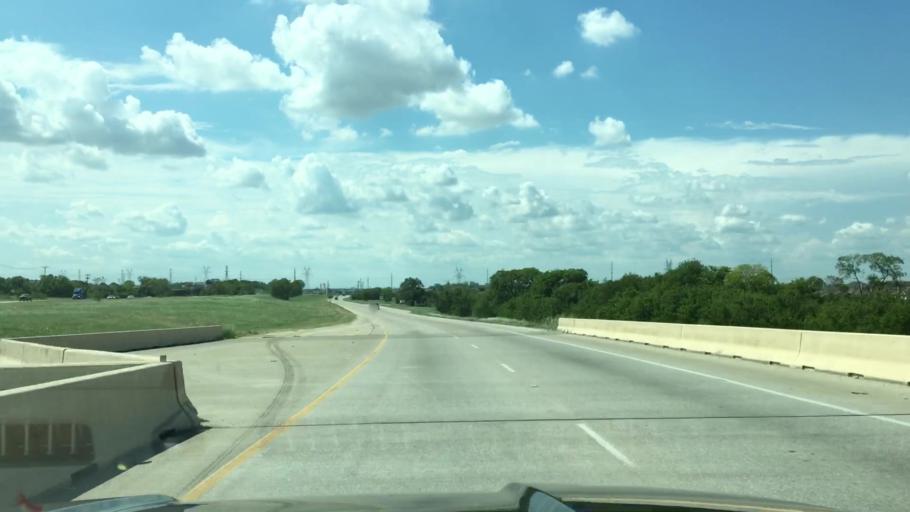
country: US
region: Texas
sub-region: Denton County
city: Roanoke
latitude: 33.0146
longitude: -97.2253
